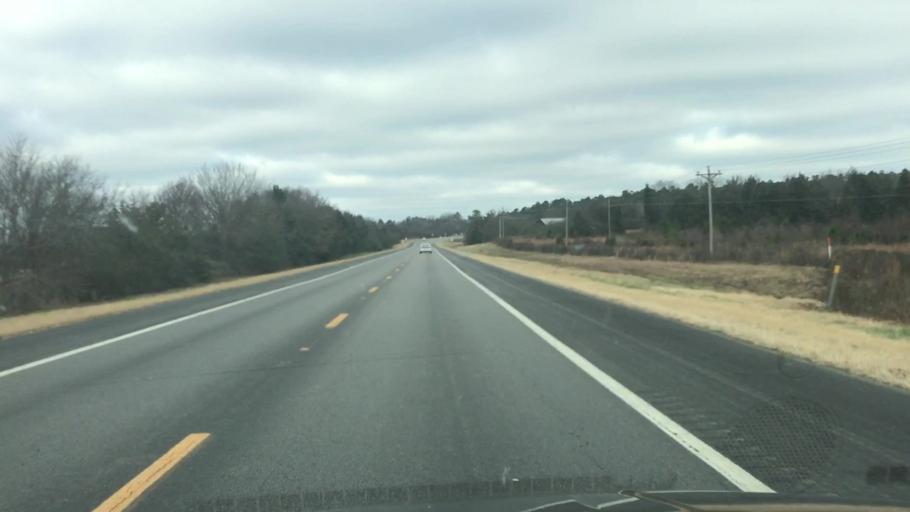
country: US
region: Arkansas
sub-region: Scott County
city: Waldron
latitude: 34.8795
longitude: -94.0992
